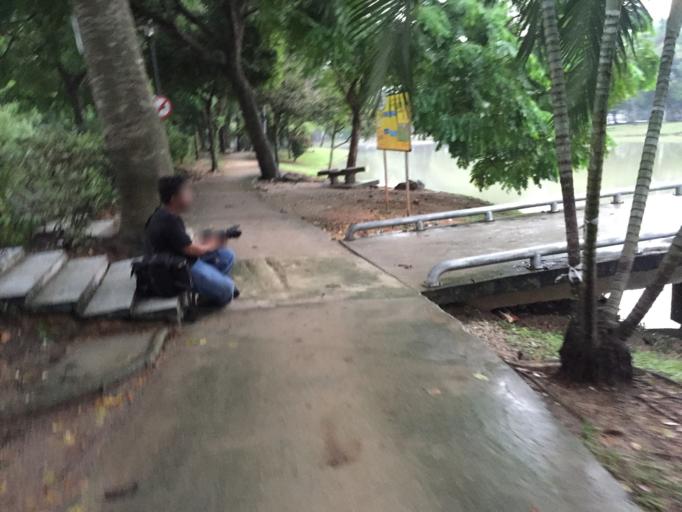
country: MY
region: Selangor
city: Klang
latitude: 2.9892
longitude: 101.4440
